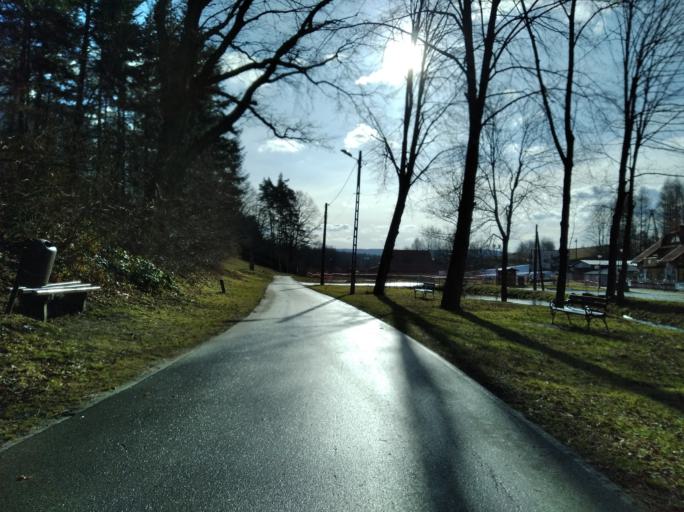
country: PL
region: Subcarpathian Voivodeship
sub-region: Powiat strzyzowski
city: Strzyzow
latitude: 49.8798
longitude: 21.7762
